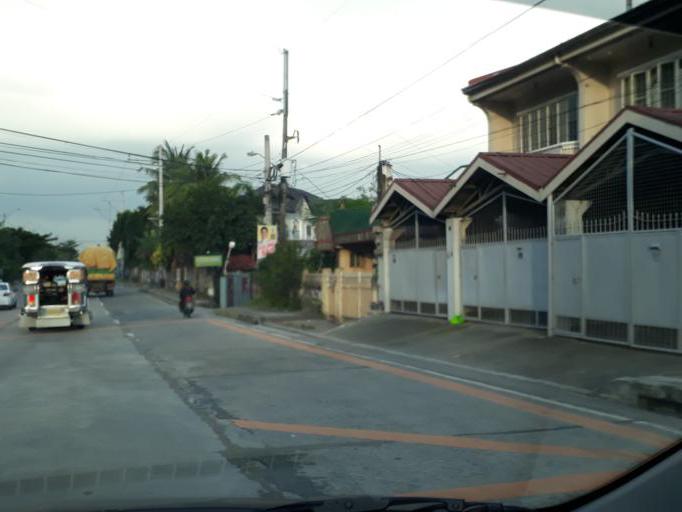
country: PH
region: Calabarzon
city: Bagong Pagasa
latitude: 14.6723
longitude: 121.0453
